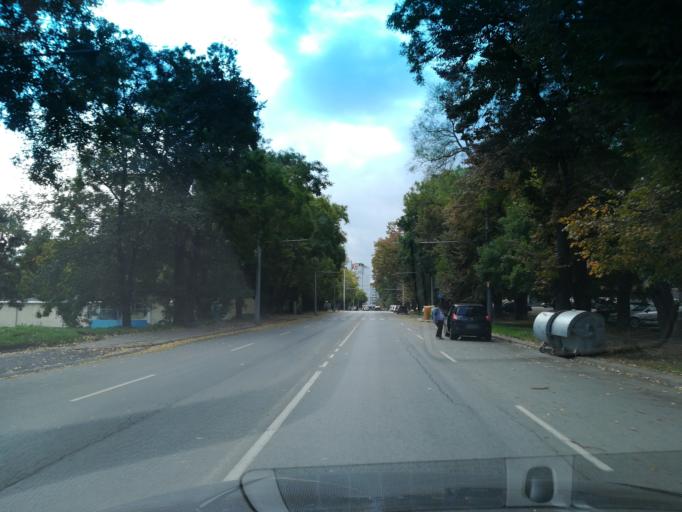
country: BG
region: Stara Zagora
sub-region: Obshtina Stara Zagora
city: Stara Zagora
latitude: 42.4406
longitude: 25.6329
